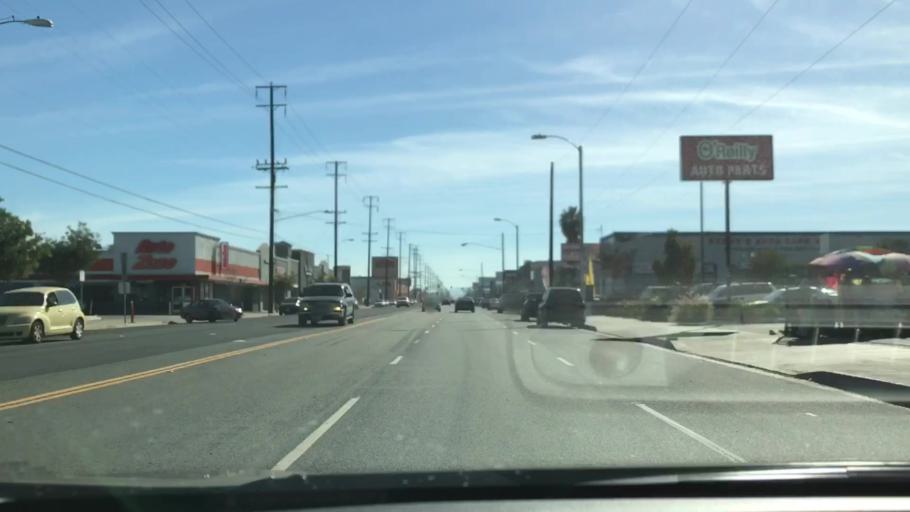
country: US
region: California
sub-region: Los Angeles County
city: Alondra Park
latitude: 33.8981
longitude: -118.3266
